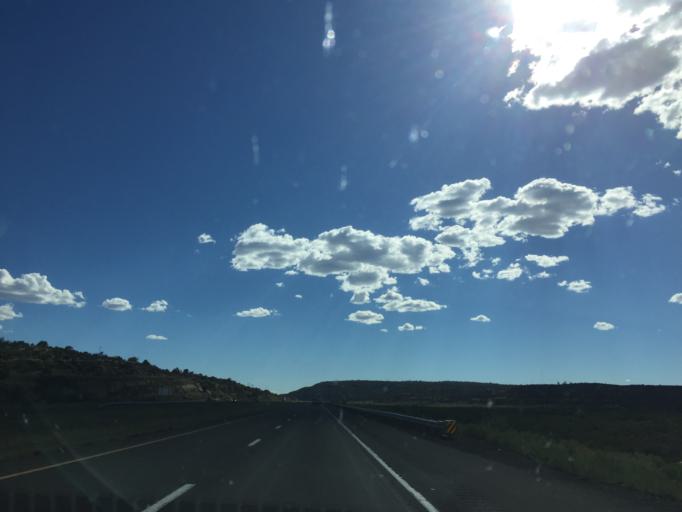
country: US
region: New Mexico
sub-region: McKinley County
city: Gallup
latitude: 35.4754
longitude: -108.9225
